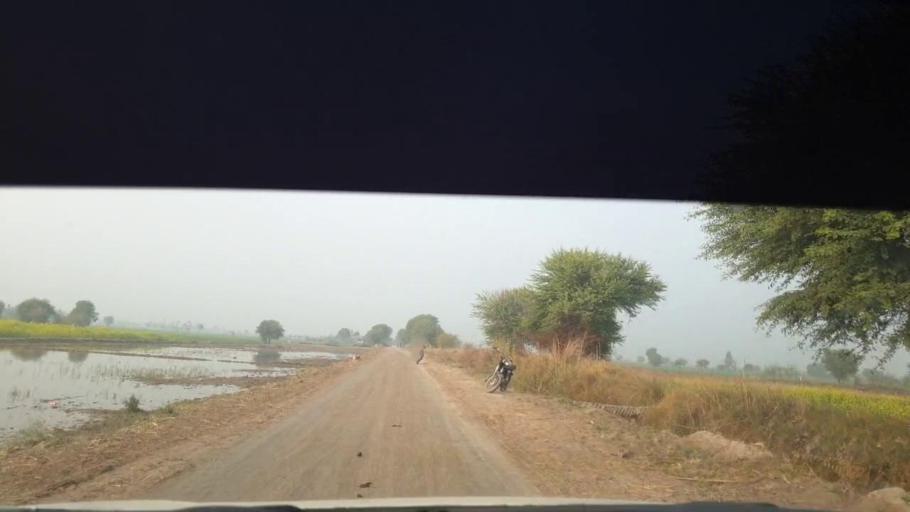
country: PK
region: Sindh
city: Berani
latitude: 25.8379
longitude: 68.8911
